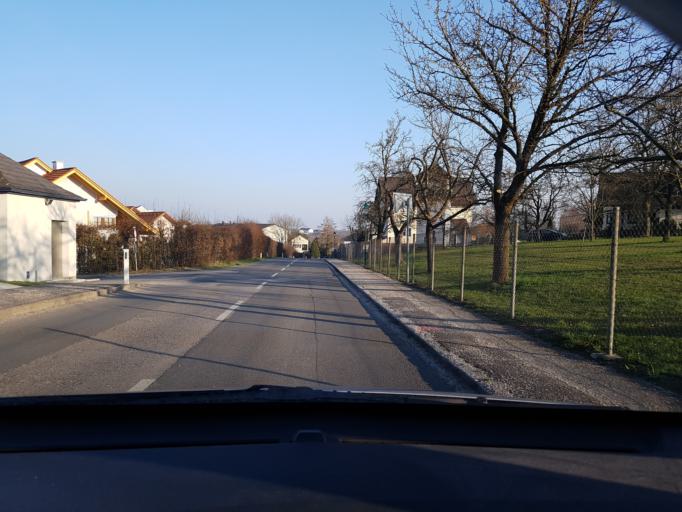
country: AT
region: Upper Austria
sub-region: Politischer Bezirk Linz-Land
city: Ansfelden
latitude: 48.1491
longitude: 14.2759
